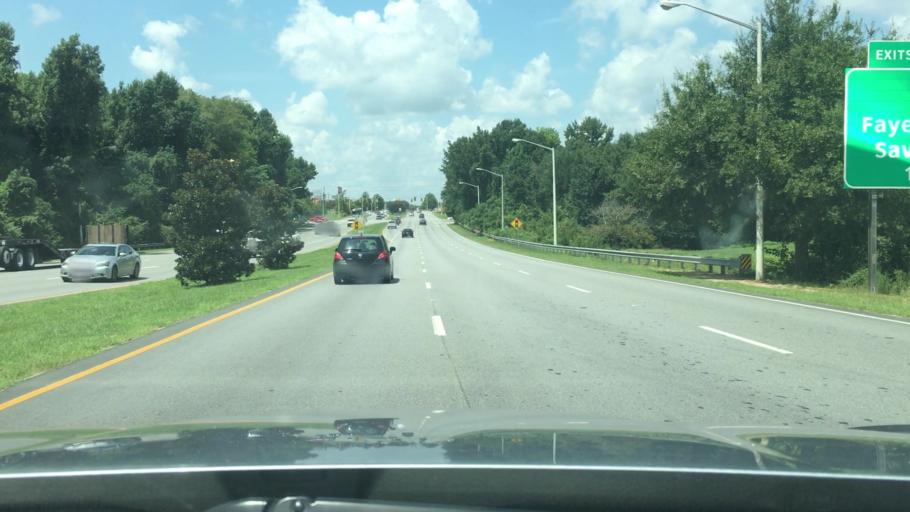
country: US
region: South Carolina
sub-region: Florence County
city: Florence
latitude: 34.1884
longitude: -79.8260
